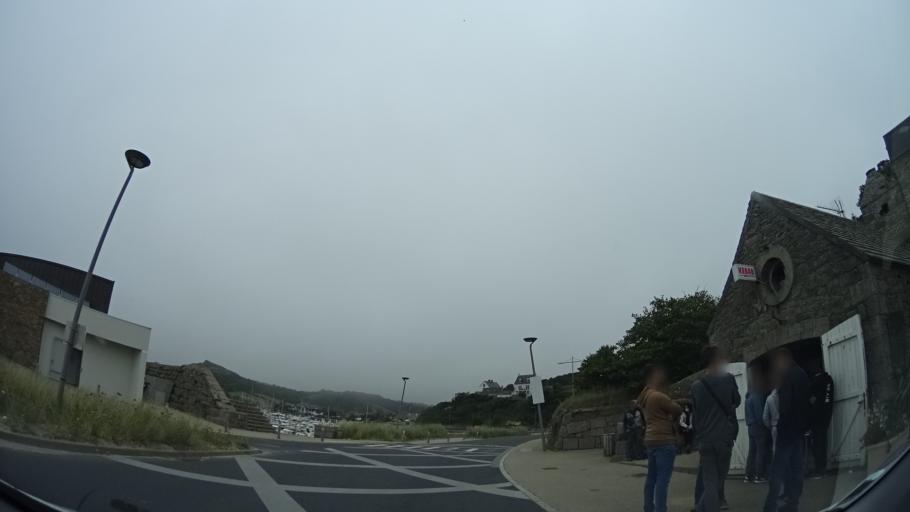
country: FR
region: Lower Normandy
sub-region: Departement de la Manche
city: Flamanville
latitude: 49.5506
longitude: -1.8618
